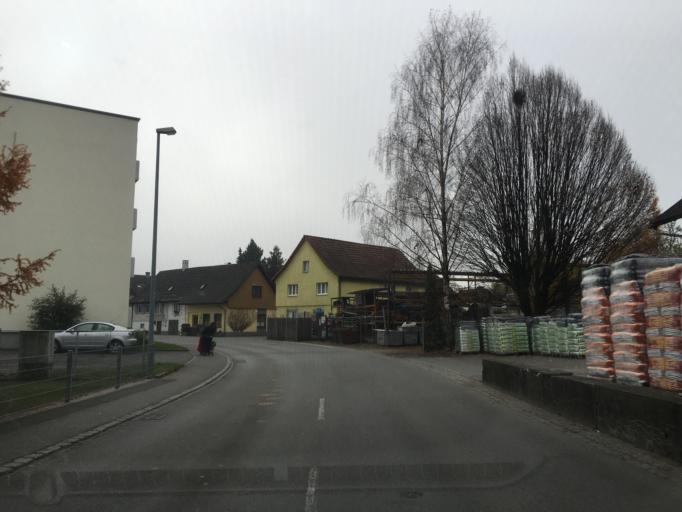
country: AT
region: Vorarlberg
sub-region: Politischer Bezirk Dornbirn
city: Lustenau
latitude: 47.4275
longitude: 9.6619
